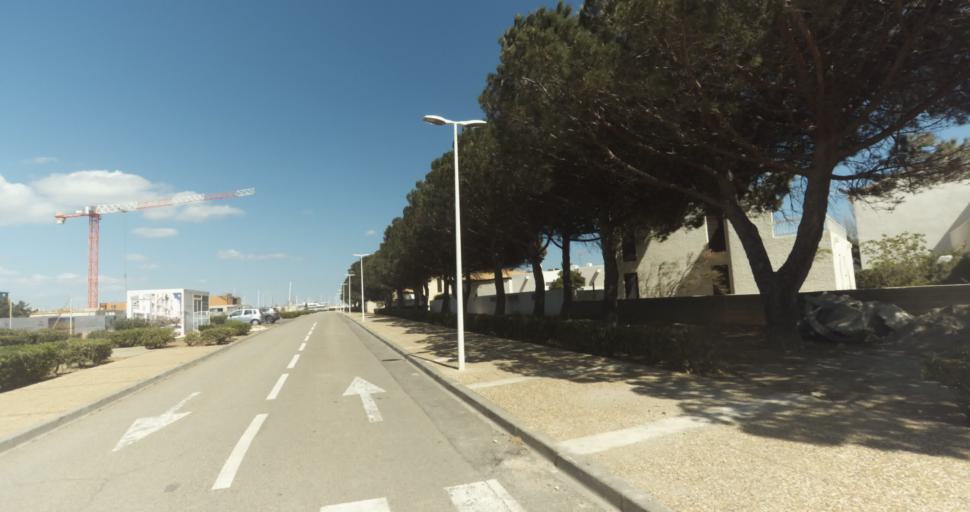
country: FR
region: Languedoc-Roussillon
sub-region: Departement de l'Aude
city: Leucate
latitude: 42.8616
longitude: 3.0393
